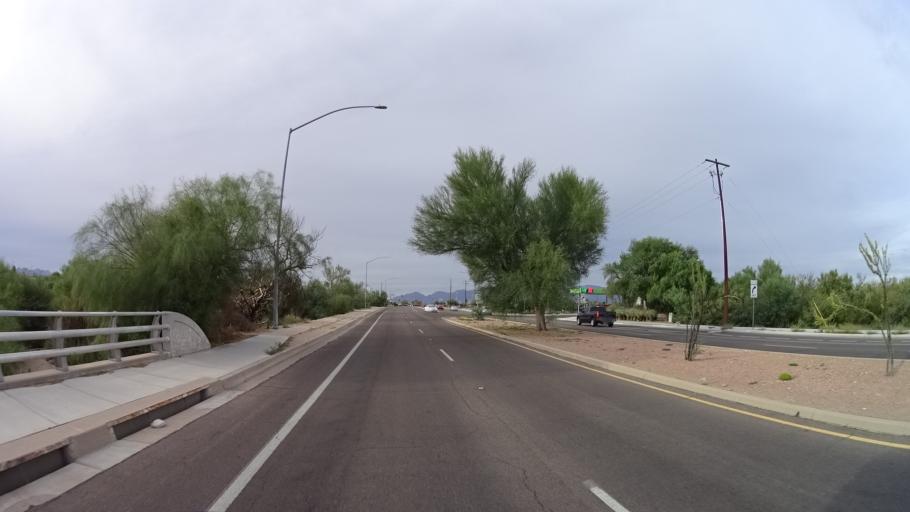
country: US
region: Arizona
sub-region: Pima County
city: South Tucson
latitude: 32.1463
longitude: -110.9350
